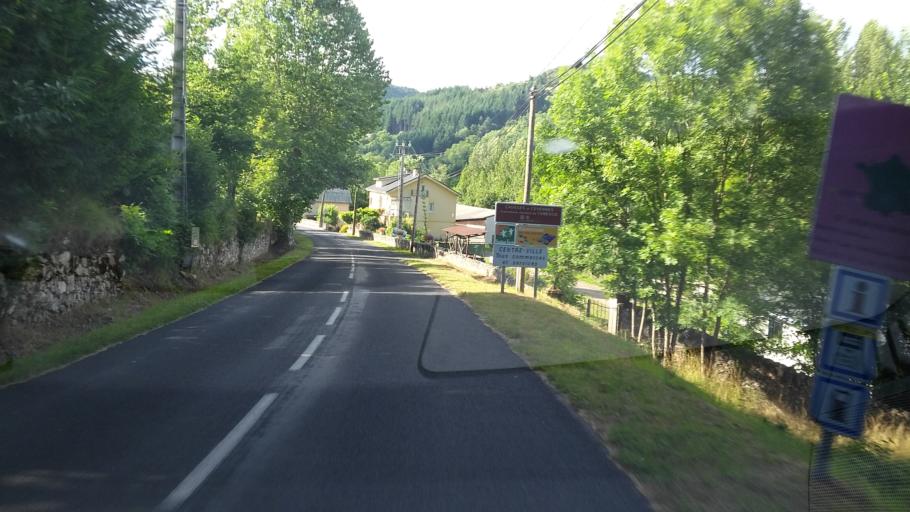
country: FR
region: Languedoc-Roussillon
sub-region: Departement de la Lozere
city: Meyrueis
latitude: 44.0187
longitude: 3.3635
